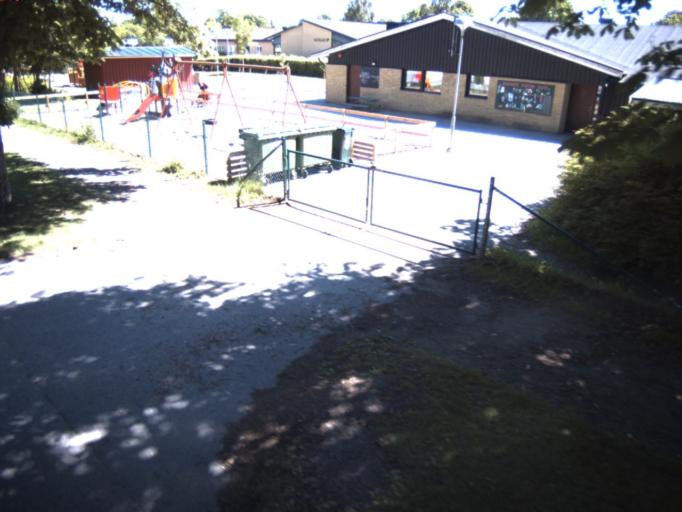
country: SE
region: Skane
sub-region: Helsingborg
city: Morarp
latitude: 56.0584
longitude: 12.8758
